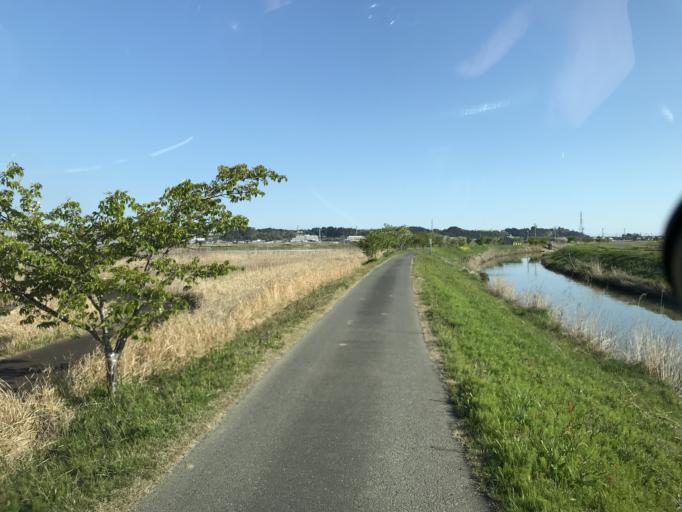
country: JP
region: Chiba
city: Omigawa
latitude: 35.8376
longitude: 140.5884
